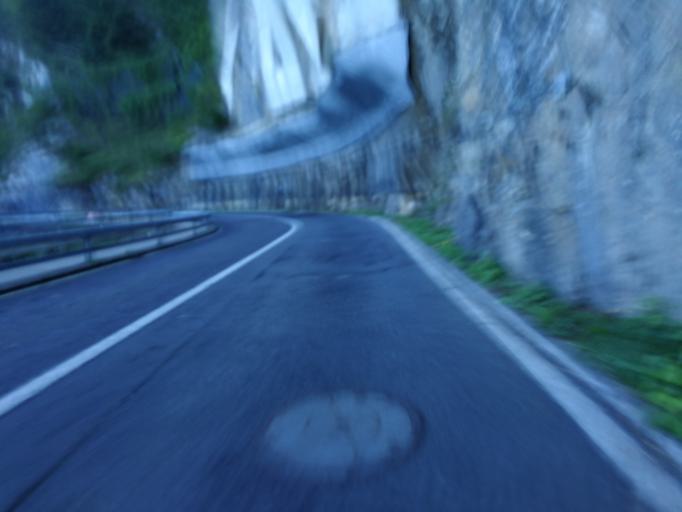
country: CH
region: Lucerne
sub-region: Lucerne-Land District
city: Vitznau
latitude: 46.9962
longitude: 8.4756
